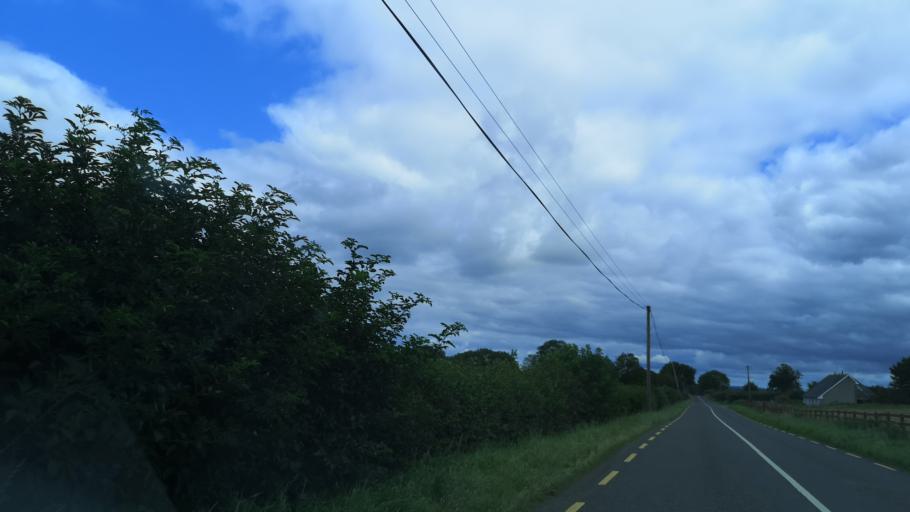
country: IE
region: Leinster
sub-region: Uibh Fhaili
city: Ferbane
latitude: 53.2249
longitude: -7.8582
